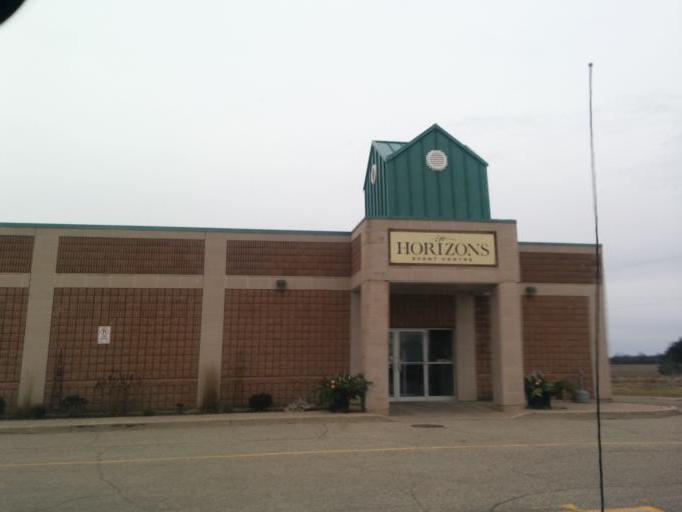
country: CA
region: Ontario
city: Orangeville
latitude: 43.9572
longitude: -80.1048
